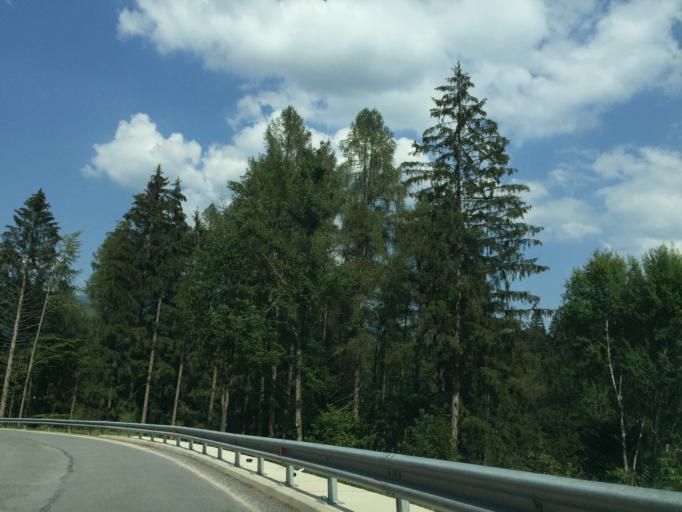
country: SI
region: Slovenj Gradec
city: Smartno pri Slovenj Gradcu
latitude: 46.4462
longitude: 15.1187
